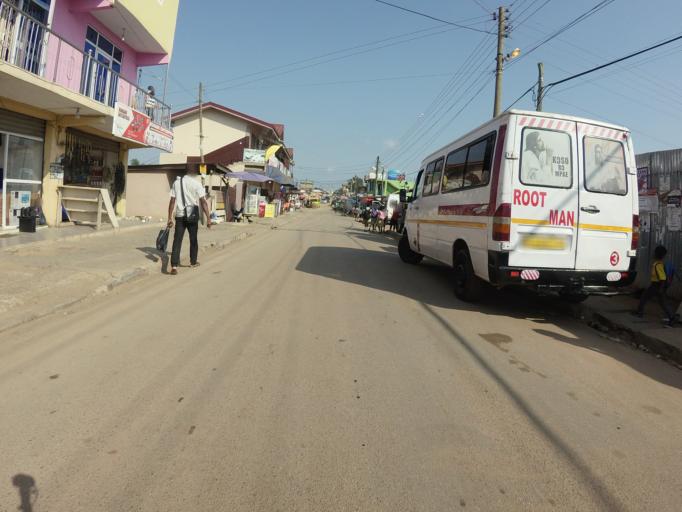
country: GH
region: Greater Accra
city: Dome
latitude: 5.6097
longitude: -0.2477
